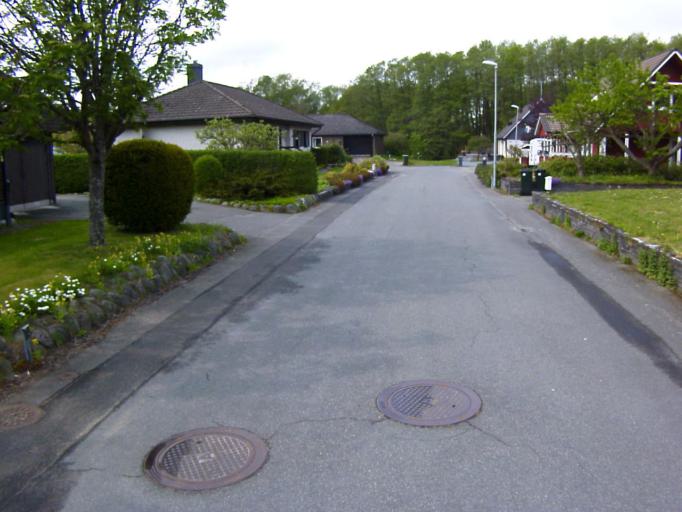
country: SE
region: Skane
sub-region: Kristianstads Kommun
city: Degeberga
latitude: 55.8256
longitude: 14.0920
